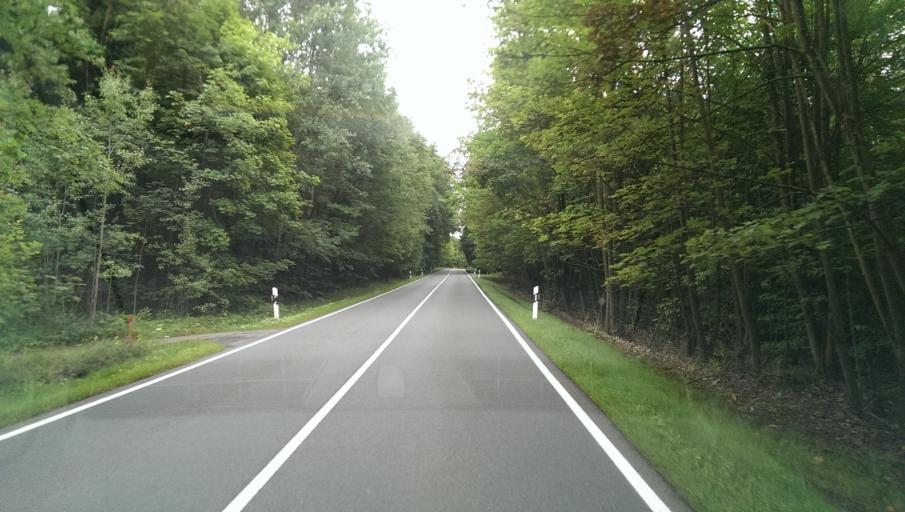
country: DE
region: Saxony
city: Pausa
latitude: 50.6048
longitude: 11.9973
